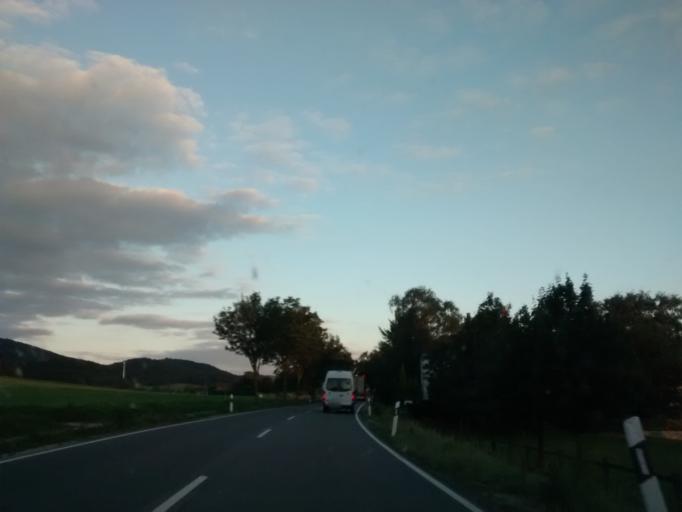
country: DE
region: North Rhine-Westphalia
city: Borgholzhausen
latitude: 52.0770
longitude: 8.3159
